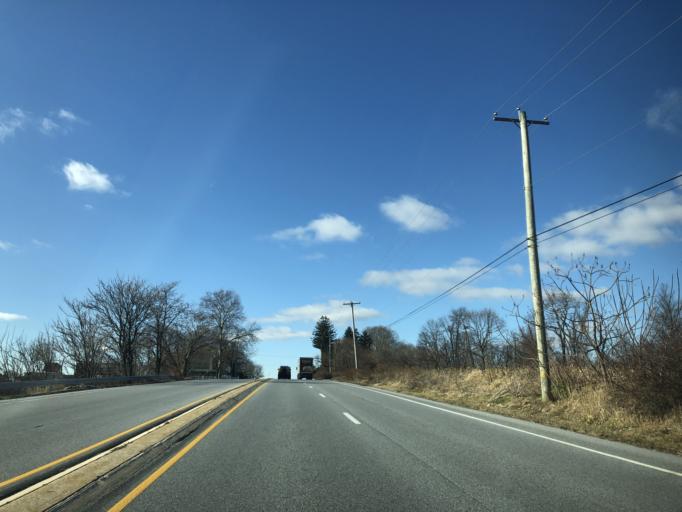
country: US
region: Pennsylvania
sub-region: Chester County
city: Parkesburg
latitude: 39.9822
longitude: -75.9160
